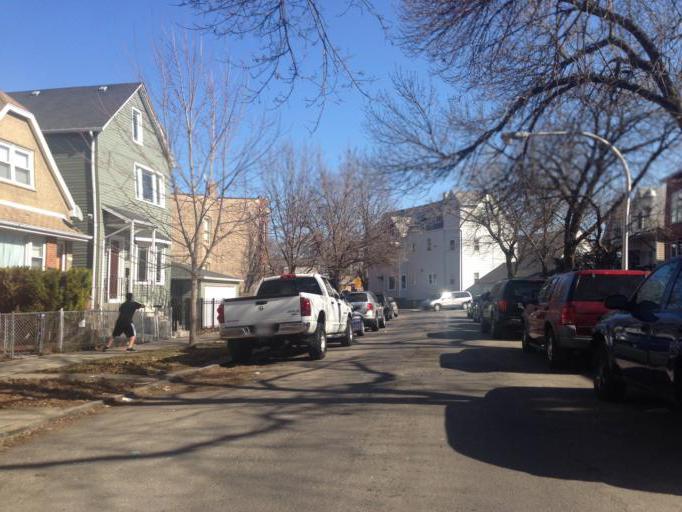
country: US
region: Illinois
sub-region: Cook County
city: Lincolnwood
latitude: 41.9369
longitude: -87.7012
